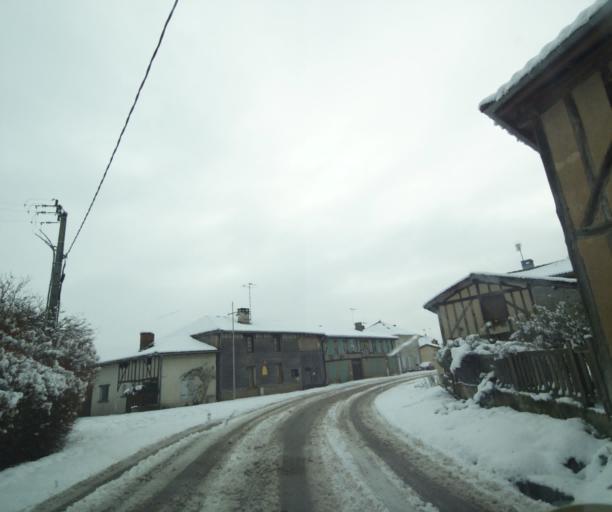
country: FR
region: Champagne-Ardenne
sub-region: Departement de la Haute-Marne
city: Montier-en-Der
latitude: 48.5166
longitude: 4.6998
